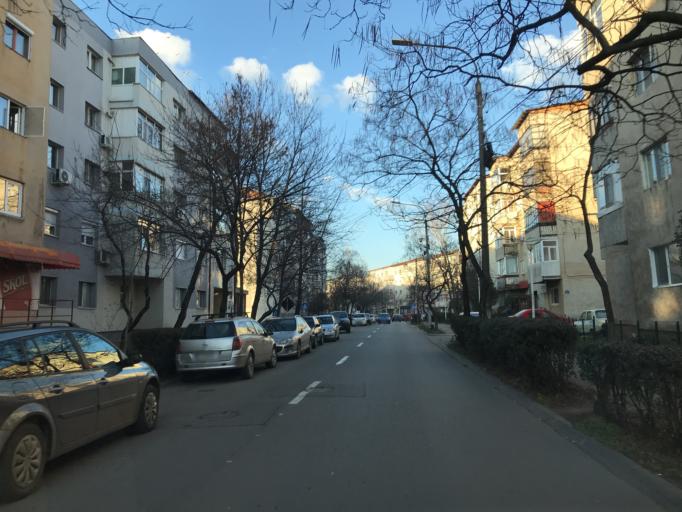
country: RO
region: Olt
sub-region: Municipiul Slatina
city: Slatina
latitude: 44.4200
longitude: 24.3814
